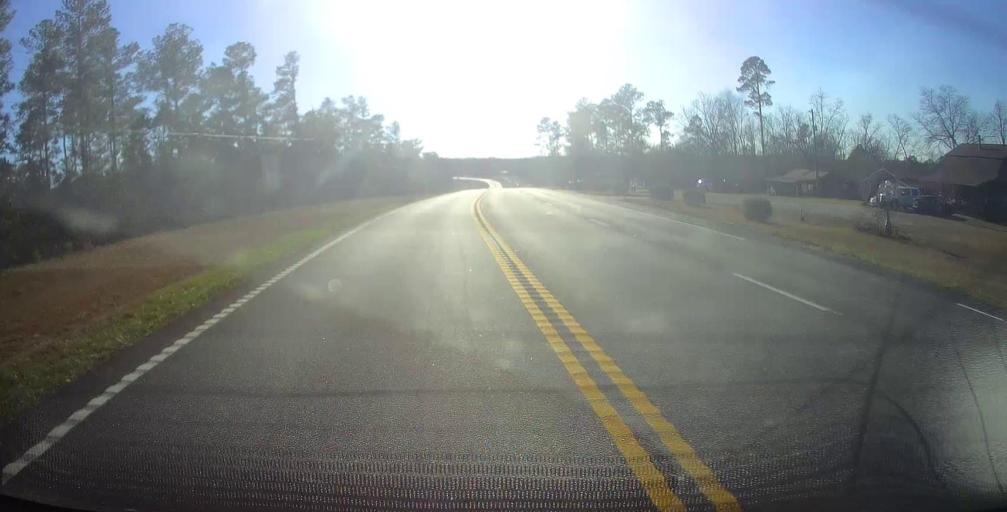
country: US
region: Georgia
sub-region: Meriwether County
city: Manchester
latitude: 32.8689
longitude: -84.6791
